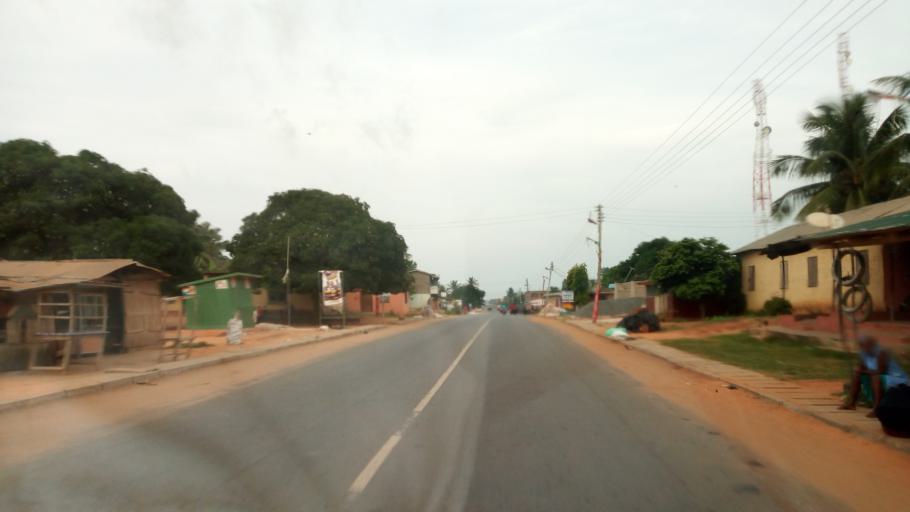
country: GH
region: Volta
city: Keta
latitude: 6.0734
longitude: 1.0347
